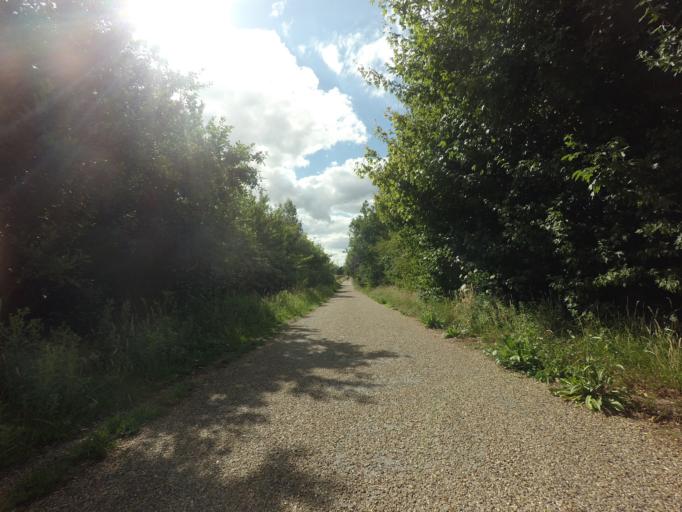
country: GB
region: England
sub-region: East Sussex
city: Hailsham
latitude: 50.8183
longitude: 0.2685
